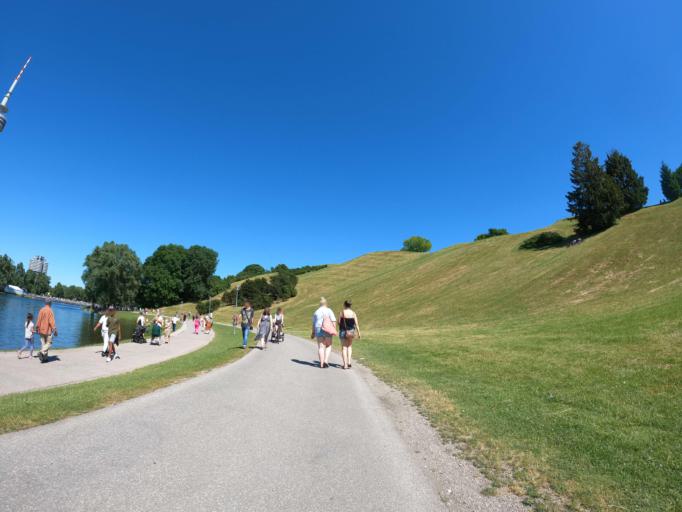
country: DE
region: Bavaria
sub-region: Upper Bavaria
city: Munich
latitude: 48.1710
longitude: 11.5506
